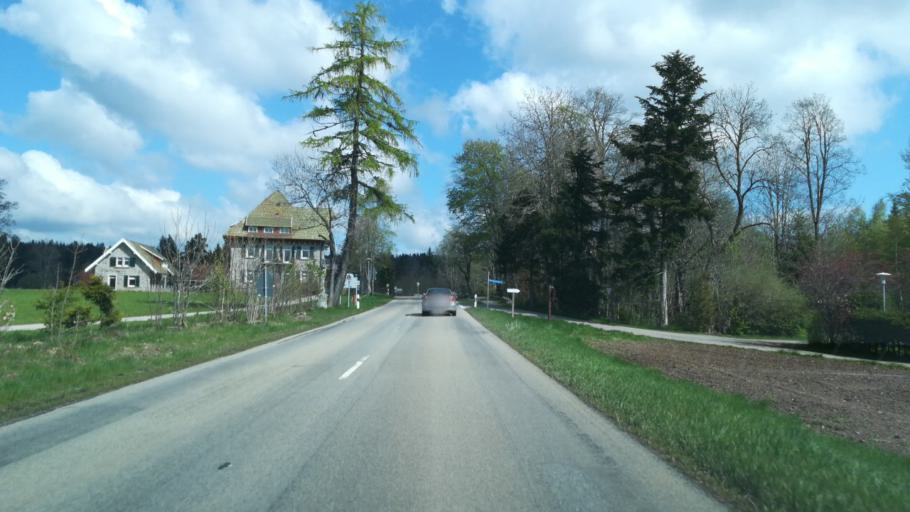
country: DE
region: Baden-Wuerttemberg
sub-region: Freiburg Region
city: Grafenhausen
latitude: 47.7911
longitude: 8.2469
